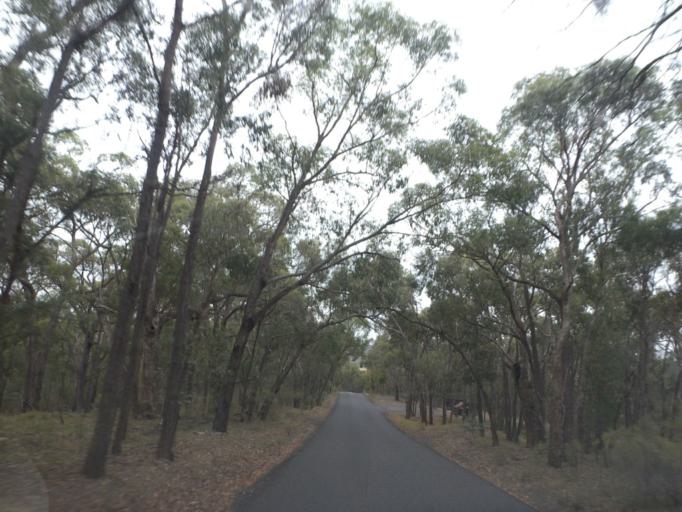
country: AU
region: Victoria
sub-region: Yarra Ranges
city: Yarra Glen
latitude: -37.6384
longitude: 145.3446
